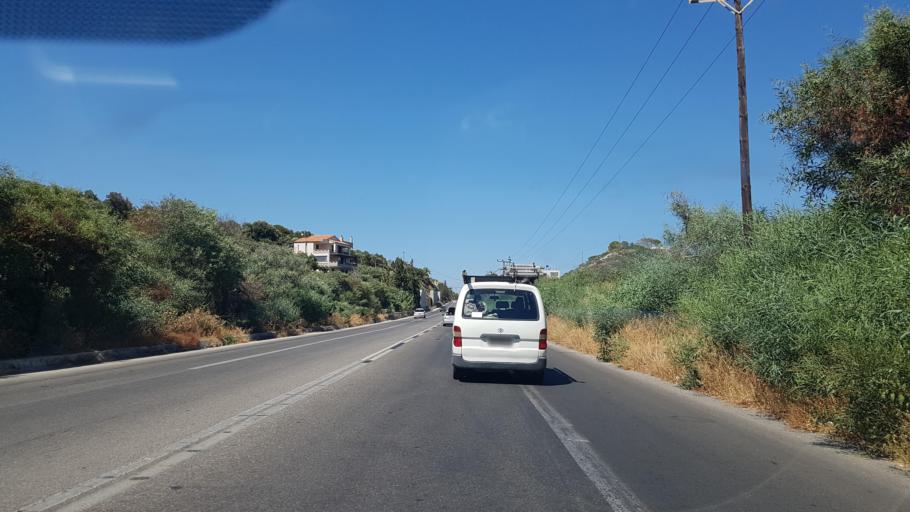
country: GR
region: Crete
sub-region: Nomos Chanias
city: Agia Marina
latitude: 35.5139
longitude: 23.9205
